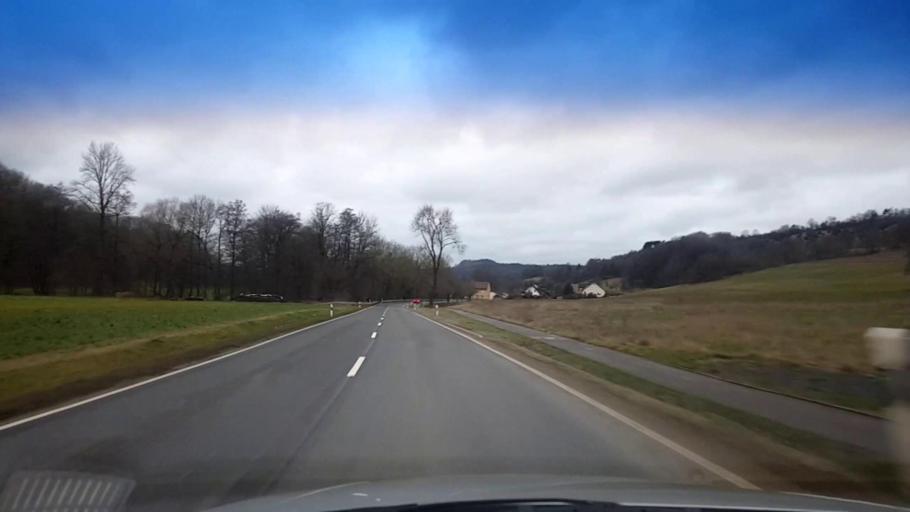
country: DE
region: Bavaria
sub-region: Upper Franconia
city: Wattendorf
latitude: 50.0658
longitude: 11.0701
